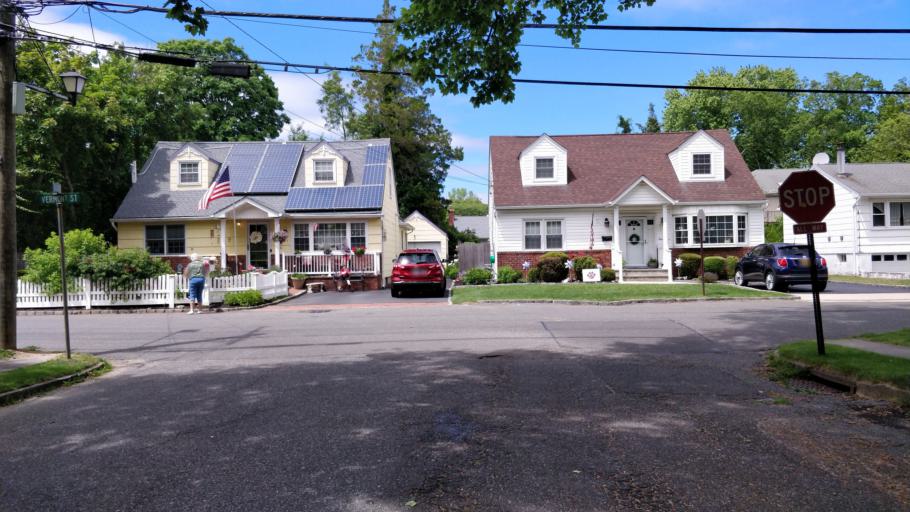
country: US
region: New York
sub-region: Suffolk County
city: South Huntington
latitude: 40.8074
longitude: -73.4038
